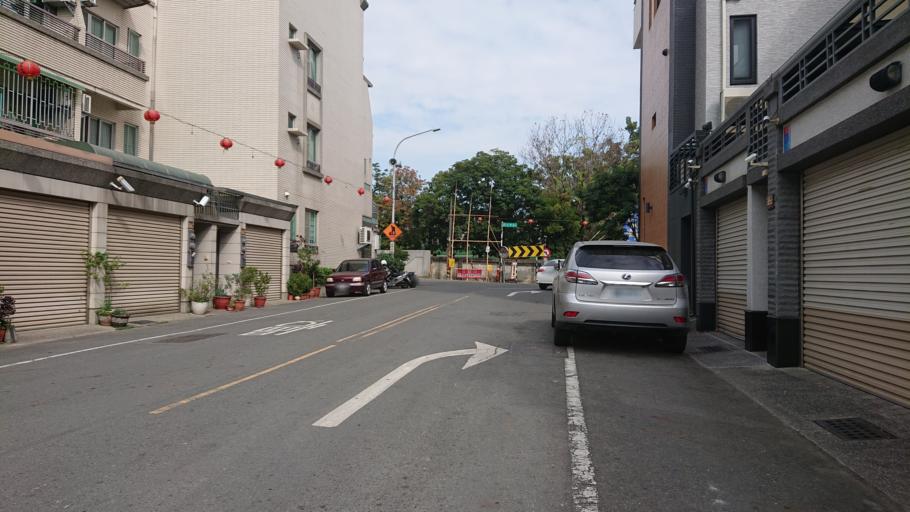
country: TW
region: Taiwan
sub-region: Tainan
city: Tainan
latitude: 23.0207
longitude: 120.2531
